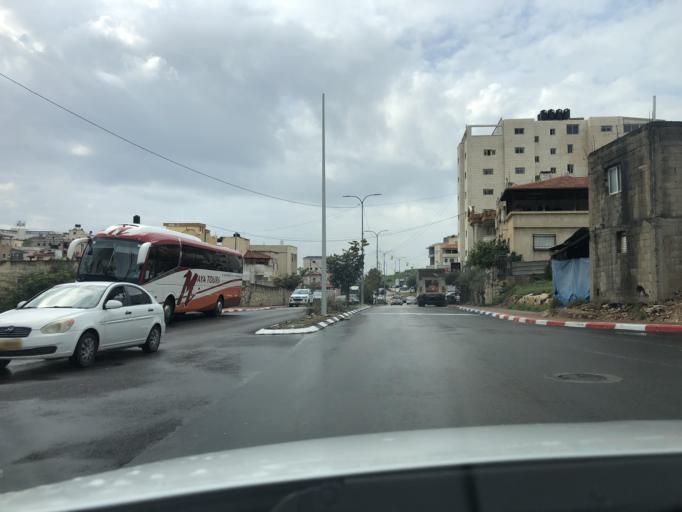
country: IL
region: Central District
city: Kafr Qasim
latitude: 32.1114
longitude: 34.9700
